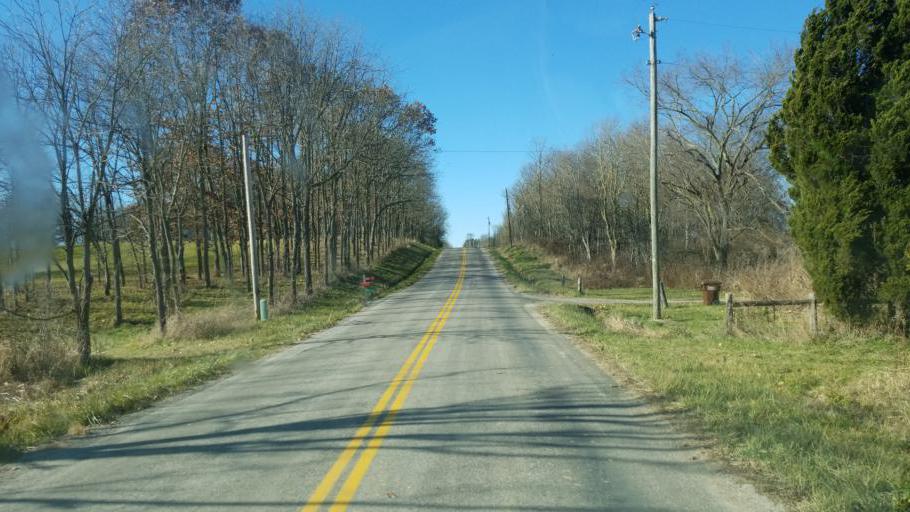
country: US
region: Ohio
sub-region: Ashland County
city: Ashland
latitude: 40.9533
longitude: -82.3785
